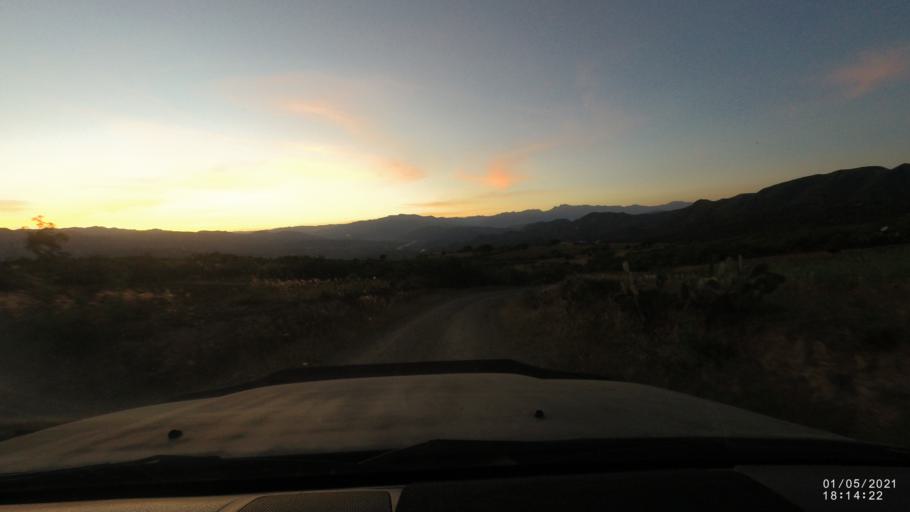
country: BO
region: Cochabamba
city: Capinota
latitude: -17.6753
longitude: -66.2122
